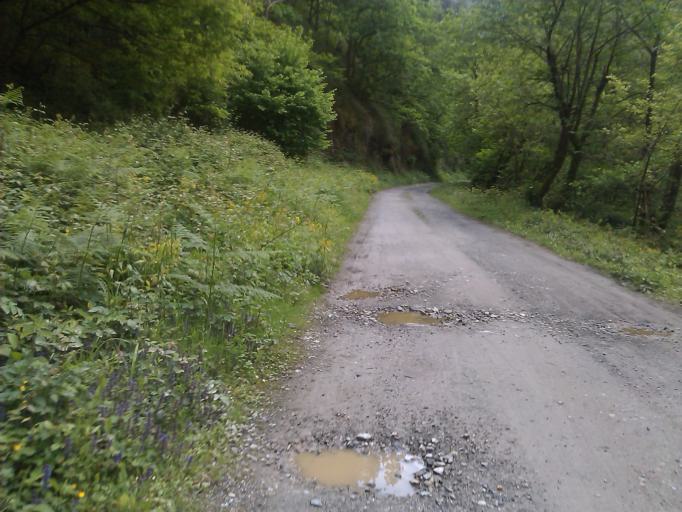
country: ES
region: Basque Country
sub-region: Provincia de Guipuzcoa
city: Berastegui
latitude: 43.1528
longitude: -1.9642
